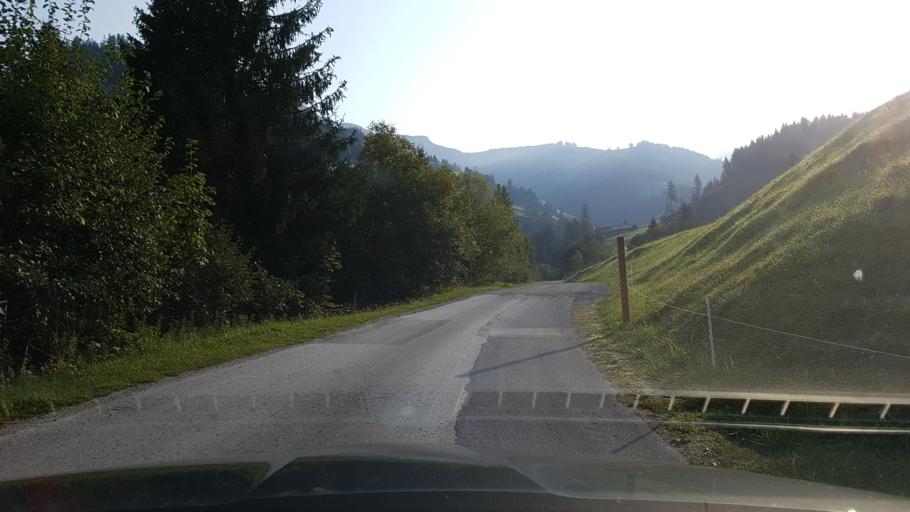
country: AT
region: Salzburg
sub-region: Politischer Bezirk Sankt Johann im Pongau
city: Sankt Johann im Pongau
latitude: 47.2761
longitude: 13.2284
